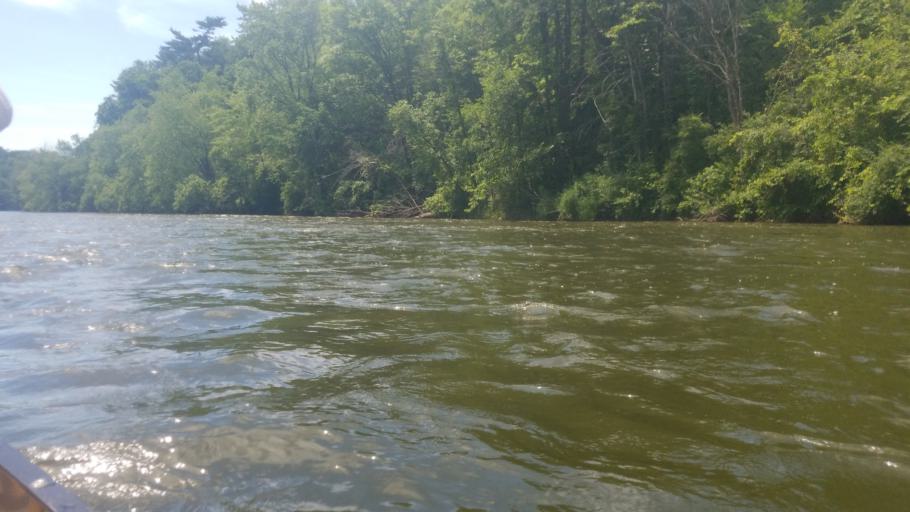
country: US
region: Wisconsin
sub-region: Dunn County
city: Menomonie
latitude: 44.8684
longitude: -91.9429
